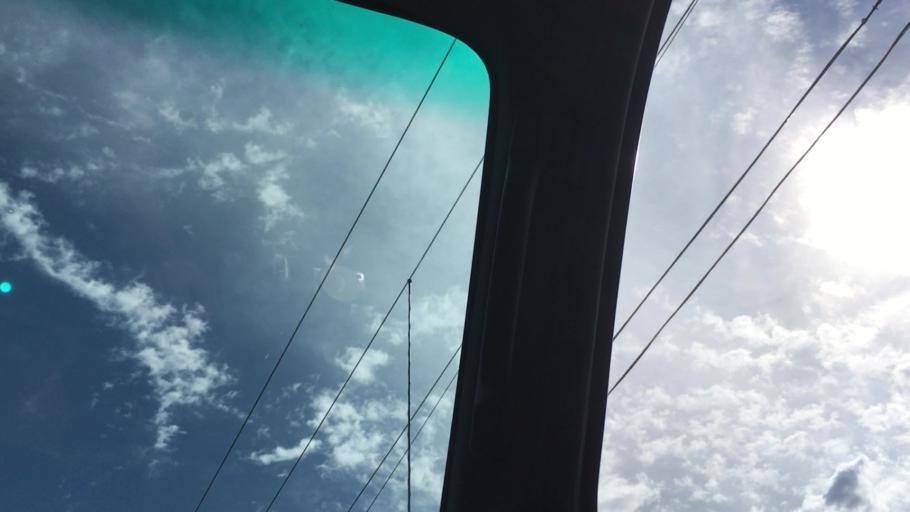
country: US
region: Maryland
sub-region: Worcester County
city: Pocomoke City
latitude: 38.0601
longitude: -75.5510
